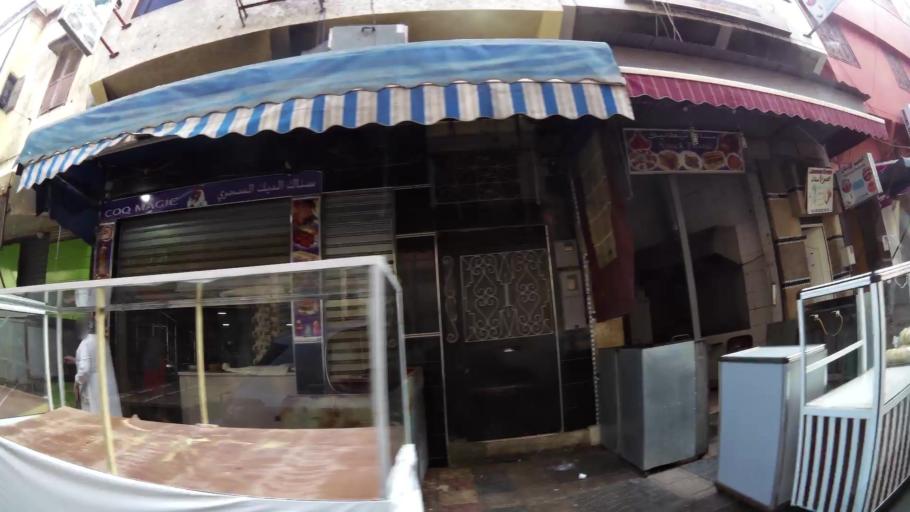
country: MA
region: Gharb-Chrarda-Beni Hssen
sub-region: Kenitra Province
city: Kenitra
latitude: 34.2639
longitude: -6.5639
